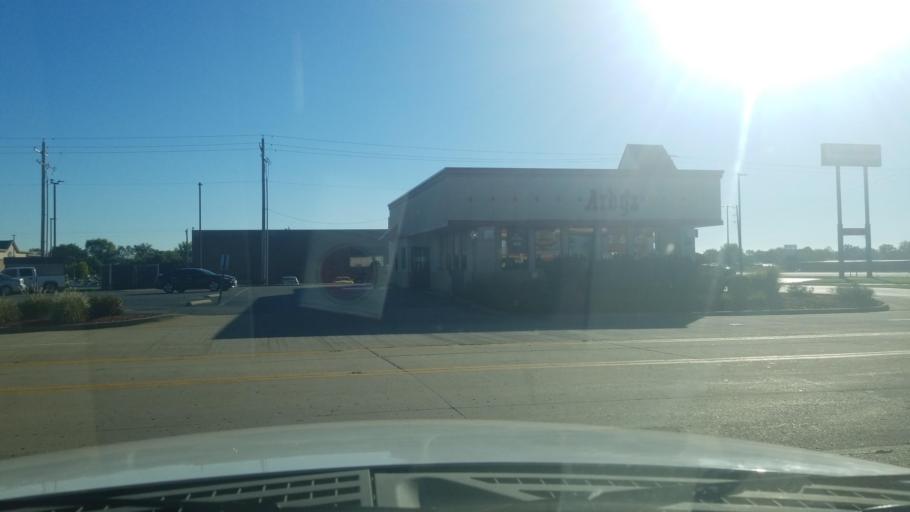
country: US
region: Illinois
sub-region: Williamson County
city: Marion
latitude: 37.7417
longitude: -88.9481
